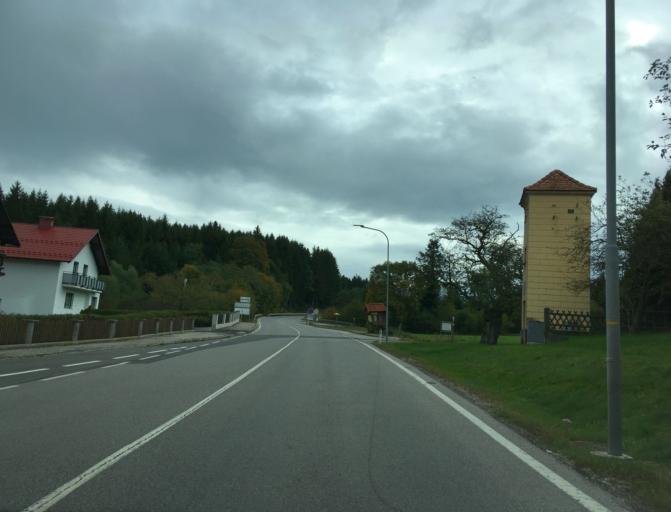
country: AT
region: Lower Austria
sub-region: Politischer Bezirk Neunkirchen
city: Thomasberg
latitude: 47.5469
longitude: 16.1450
